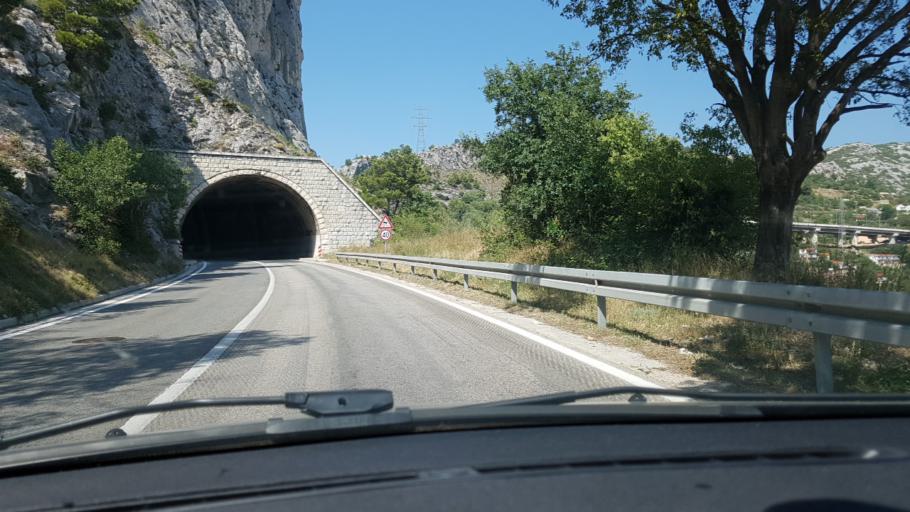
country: HR
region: Splitsko-Dalmatinska
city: Klis
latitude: 43.5595
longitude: 16.5263
